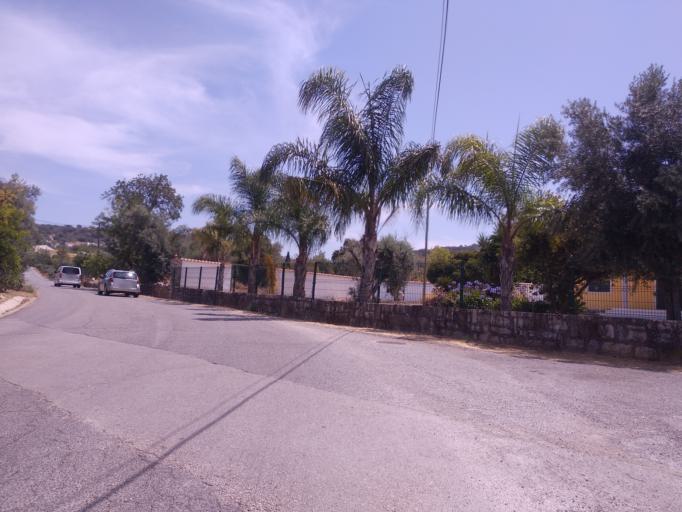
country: PT
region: Faro
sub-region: Sao Bras de Alportel
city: Sao Bras de Alportel
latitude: 37.1480
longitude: -7.9330
